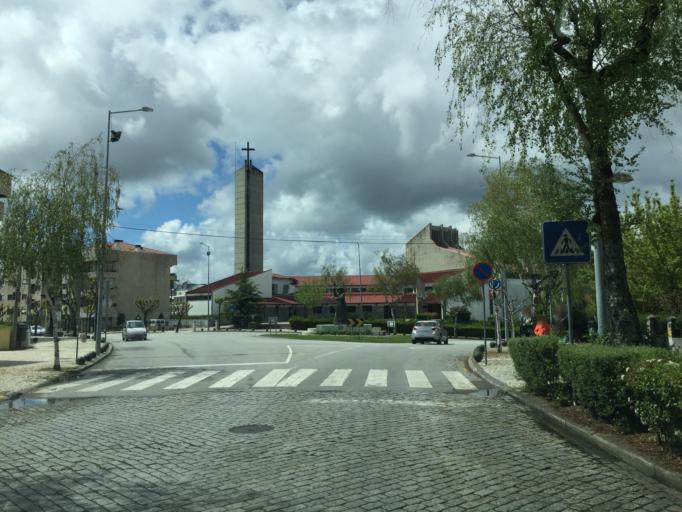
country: PT
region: Viseu
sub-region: Viseu
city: Viseu
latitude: 40.6565
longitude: -7.9200
